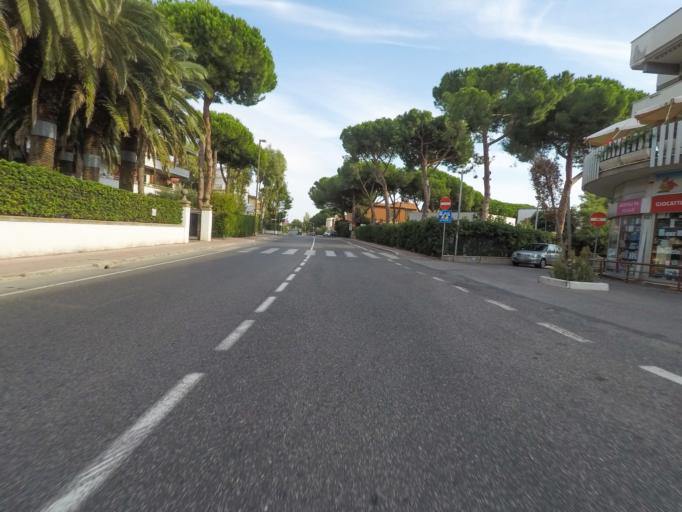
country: IT
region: Latium
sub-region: Citta metropolitana di Roma Capitale
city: Santa Marinella
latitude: 42.0329
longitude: 11.8383
